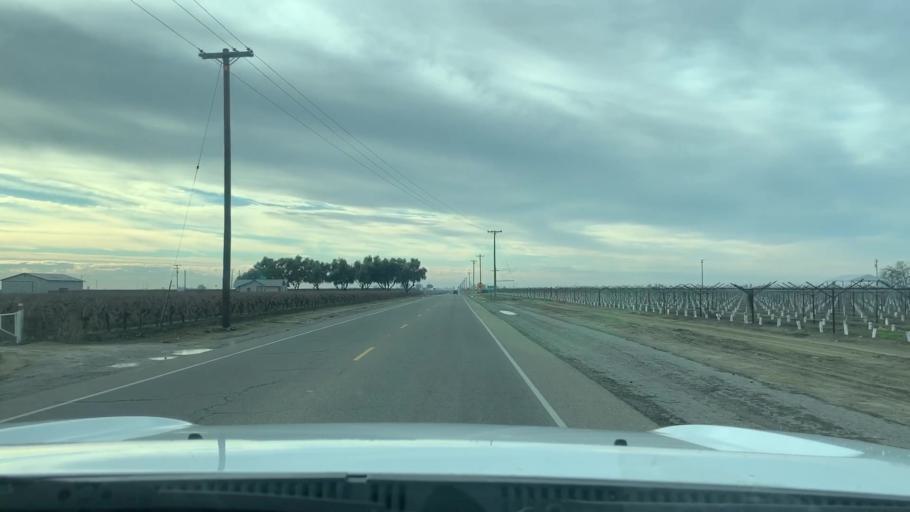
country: US
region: California
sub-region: Fresno County
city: Fowler
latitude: 36.6055
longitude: -119.6968
